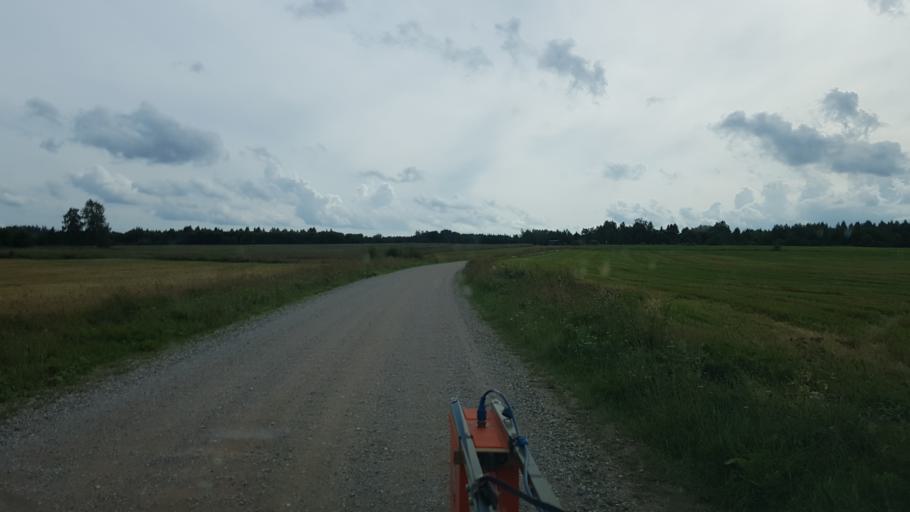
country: RU
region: Pskov
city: Pechory
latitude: 57.8027
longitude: 27.5062
